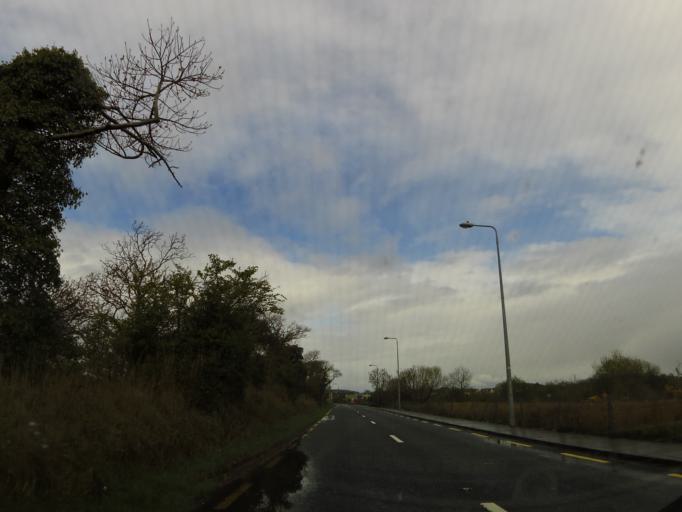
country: IE
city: Ballisodare
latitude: 54.2045
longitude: -8.5031
